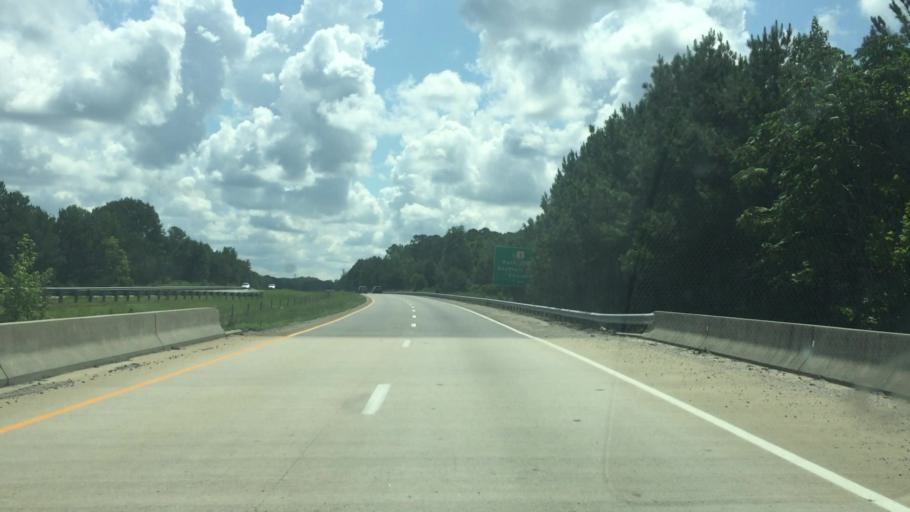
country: US
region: North Carolina
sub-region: Richmond County
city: Cordova
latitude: 34.9208
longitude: -79.8124
